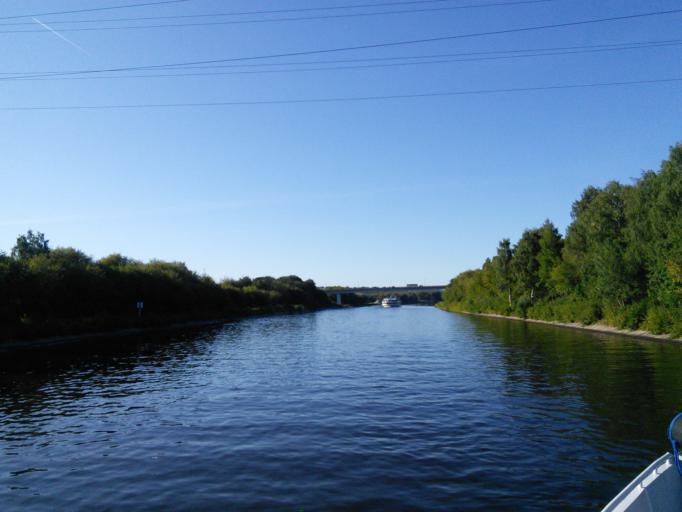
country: RU
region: Moskovskaya
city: Yakhroma
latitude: 56.2896
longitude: 37.4958
